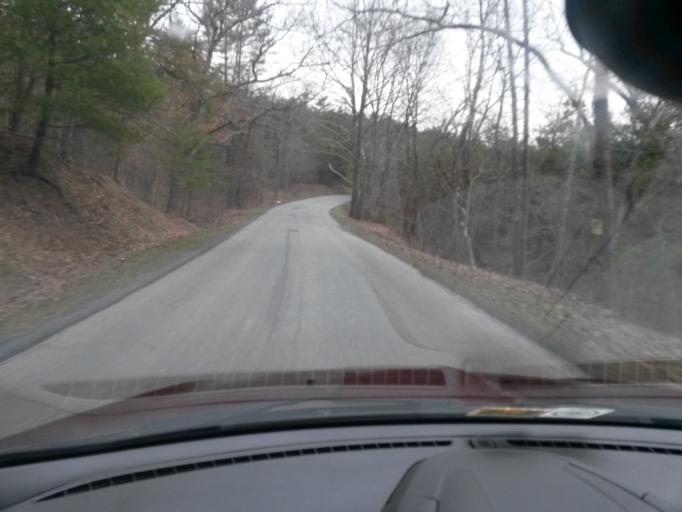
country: US
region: Virginia
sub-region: Bath County
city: Warm Springs
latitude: 38.0298
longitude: -79.8588
